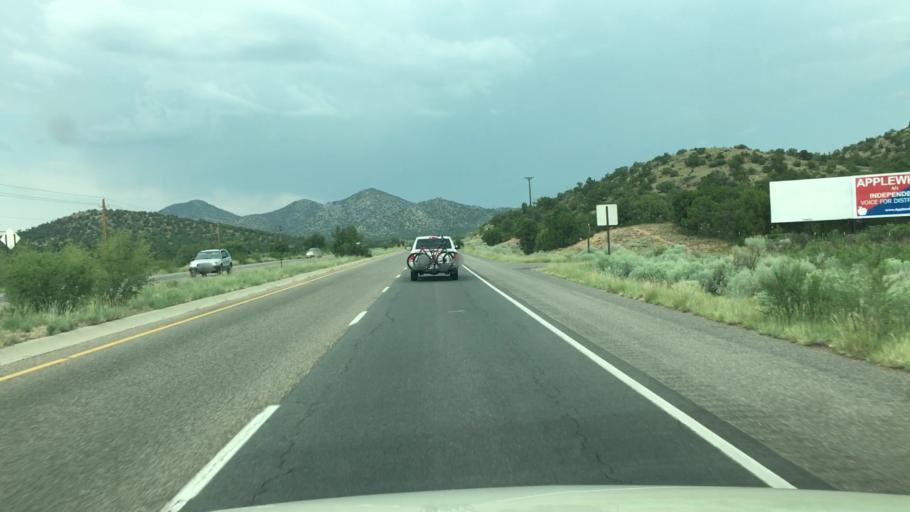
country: US
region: New Mexico
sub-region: Santa Fe County
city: Eldorado at Santa Fe
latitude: 35.5435
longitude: -105.8843
